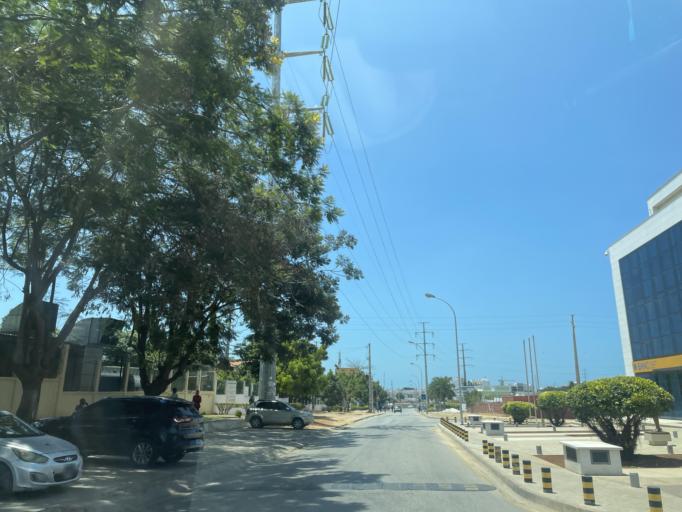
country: AO
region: Luanda
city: Luanda
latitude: -8.9073
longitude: 13.1981
